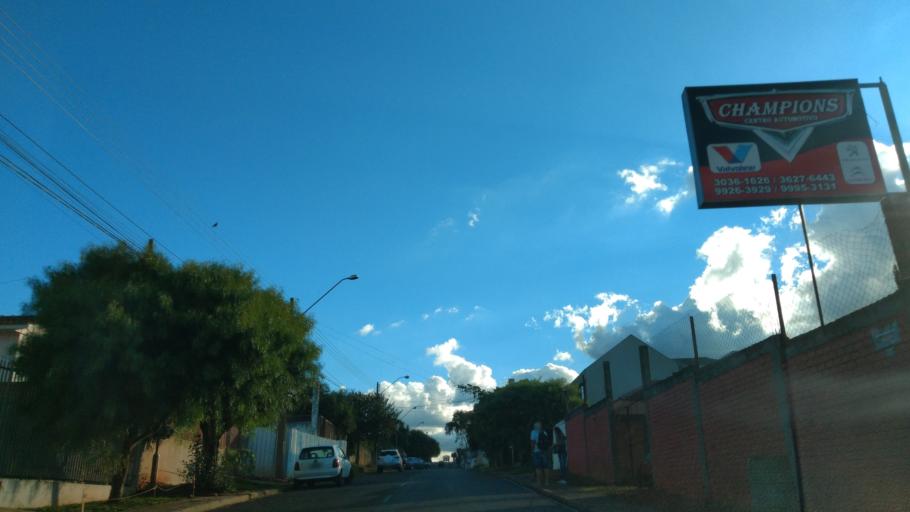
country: BR
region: Parana
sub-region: Guarapuava
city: Guarapuava
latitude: -25.3842
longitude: -51.4594
